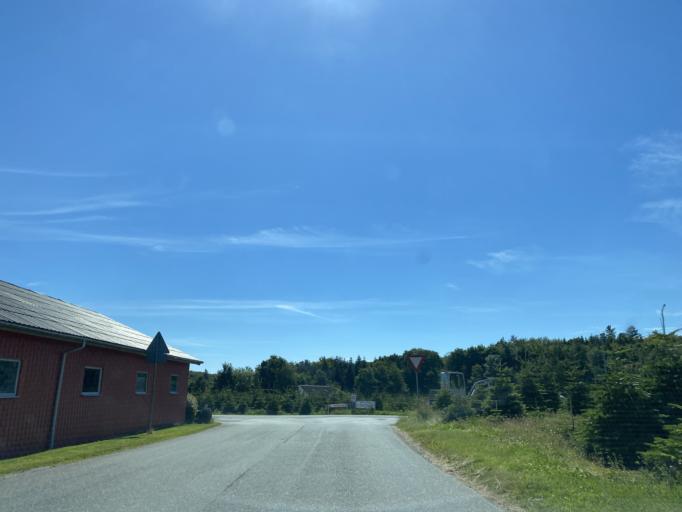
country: DK
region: South Denmark
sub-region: Vejle Kommune
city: Vejle
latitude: 55.6405
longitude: 9.5446
